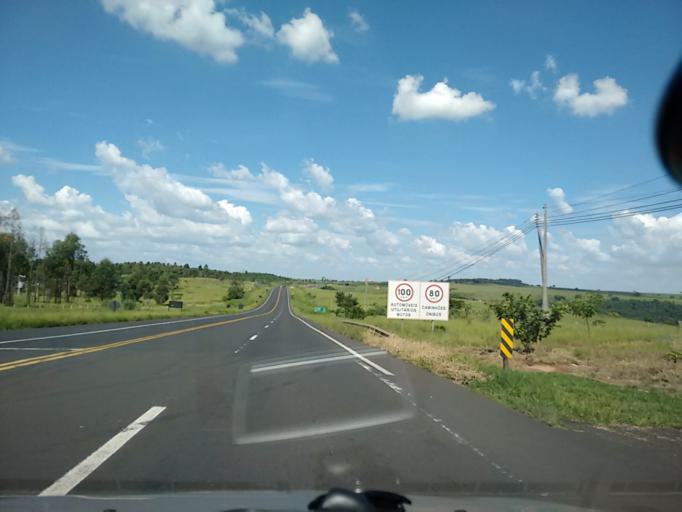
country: BR
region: Sao Paulo
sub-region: Pompeia
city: Pompeia
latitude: -22.1002
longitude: -50.2475
